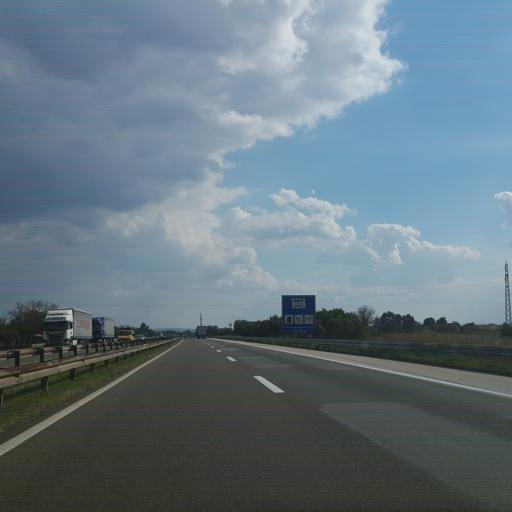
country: RS
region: Central Serbia
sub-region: Podunavski Okrug
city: Velika Plana
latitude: 44.2928
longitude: 21.0992
